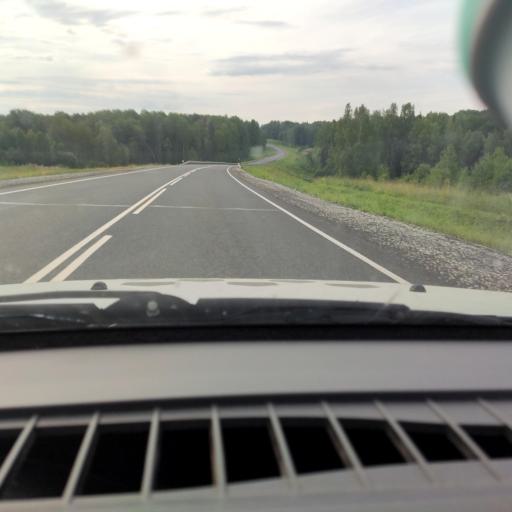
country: RU
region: Kirov
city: Kostino
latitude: 58.6482
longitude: 53.7941
